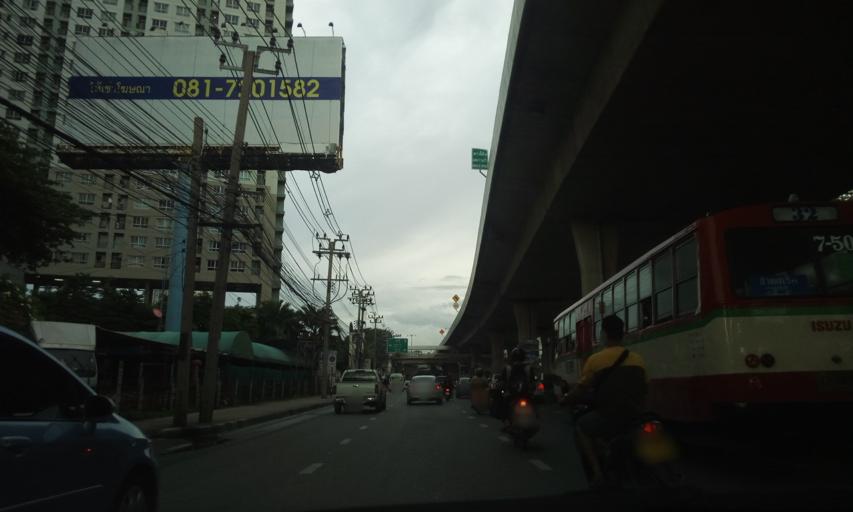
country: TH
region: Nonthaburi
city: Pak Kret
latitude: 13.9090
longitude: 100.5017
